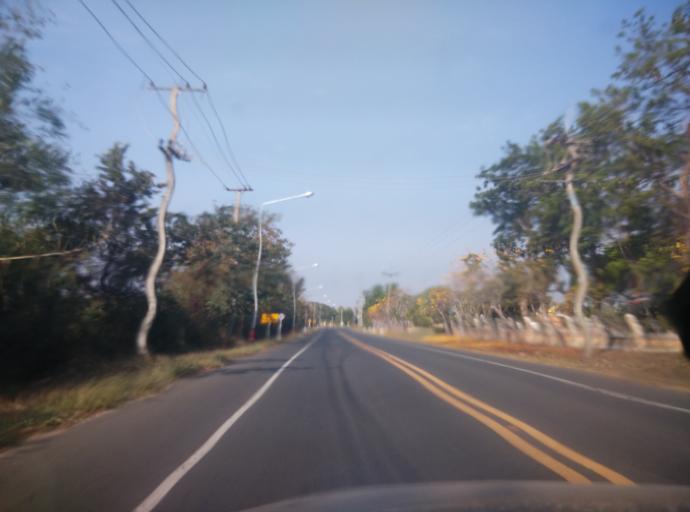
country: TH
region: Sisaket
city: Si Sa Ket
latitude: 15.1122
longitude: 104.2717
